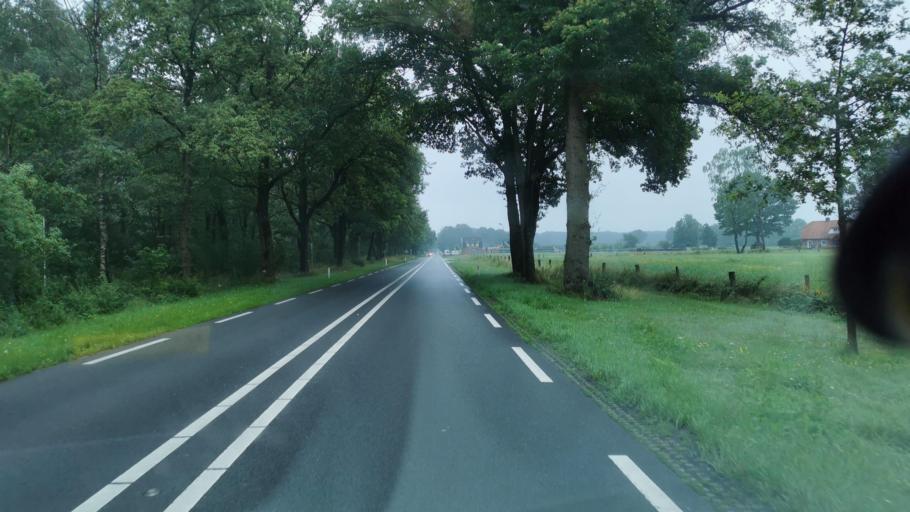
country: NL
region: Overijssel
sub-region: Gemeente Losser
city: Losser
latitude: 52.2491
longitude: 7.0258
